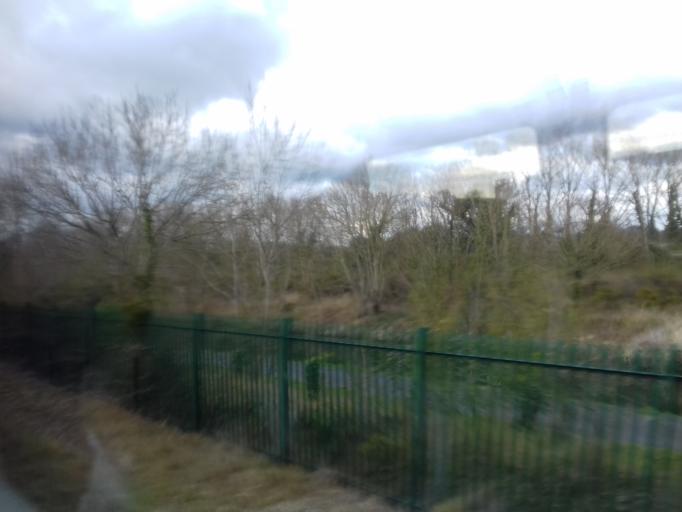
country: IE
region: Leinster
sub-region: An Iarmhi
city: An Muileann gCearr
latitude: 53.5154
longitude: -7.3257
